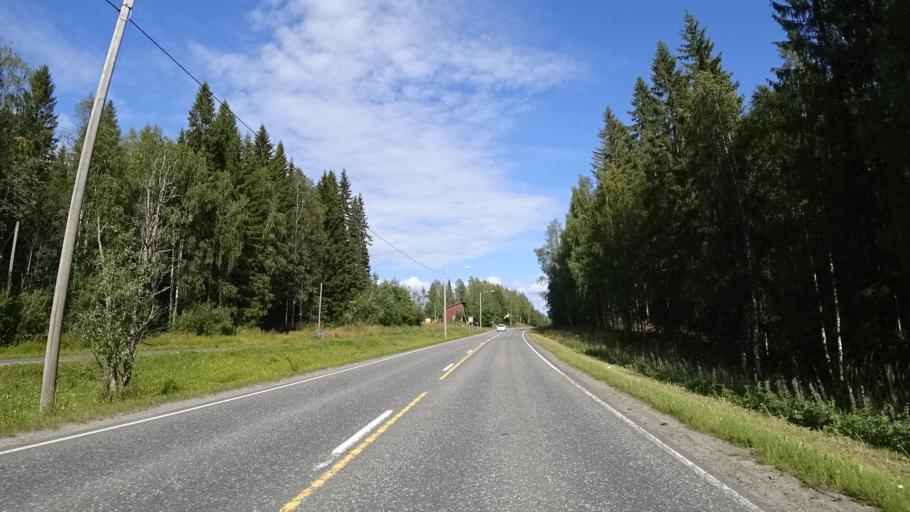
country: FI
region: North Karelia
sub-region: Joensuu
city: Eno
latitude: 62.8049
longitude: 30.1273
